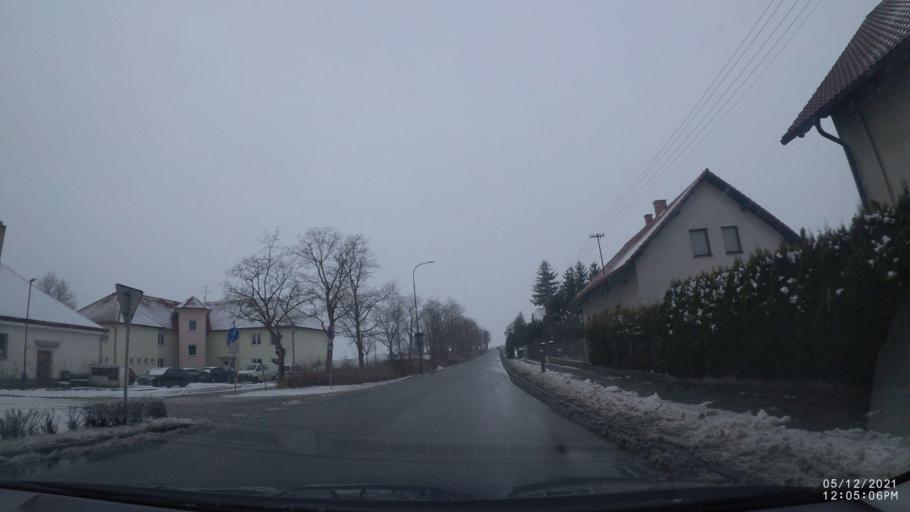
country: CZ
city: Ceske Mezirici
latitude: 50.2867
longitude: 16.0427
